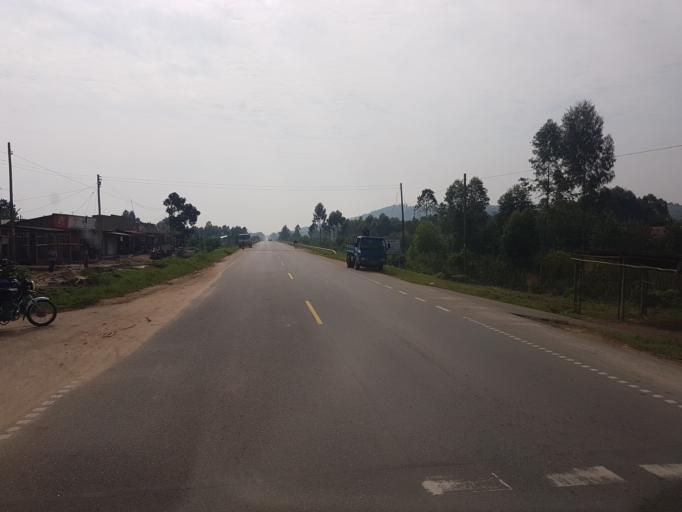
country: UG
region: Western Region
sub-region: Sheema District
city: Kibingo
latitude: -0.6447
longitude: 30.4966
